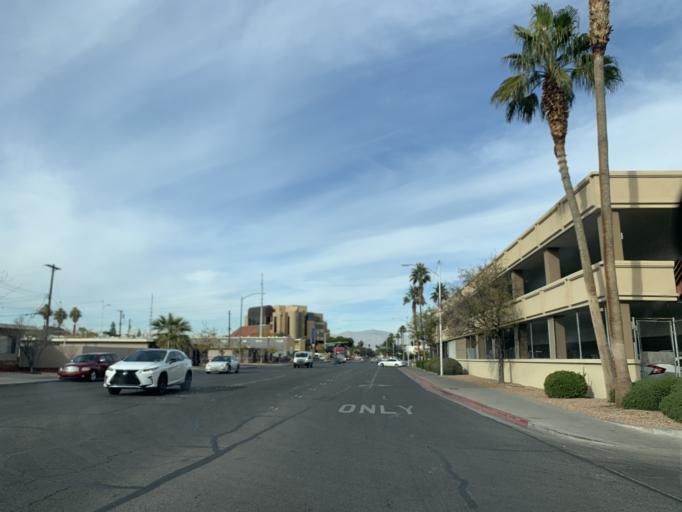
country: US
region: Nevada
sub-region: Clark County
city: Las Vegas
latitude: 36.1425
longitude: -115.1775
